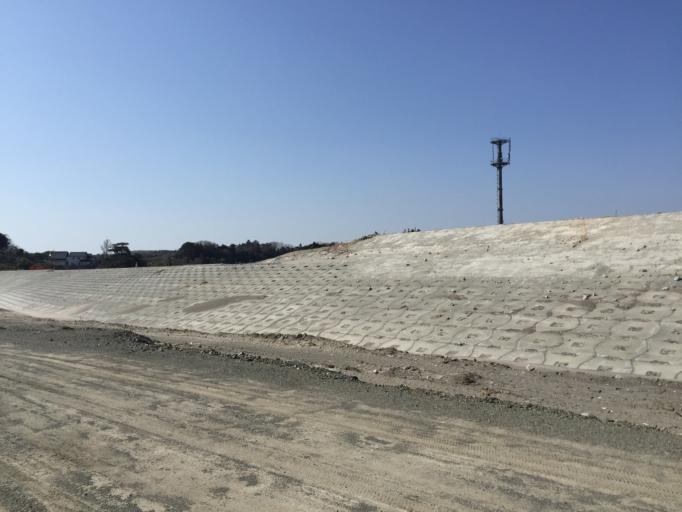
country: JP
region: Miyagi
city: Marumori
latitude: 37.7696
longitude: 140.9902
